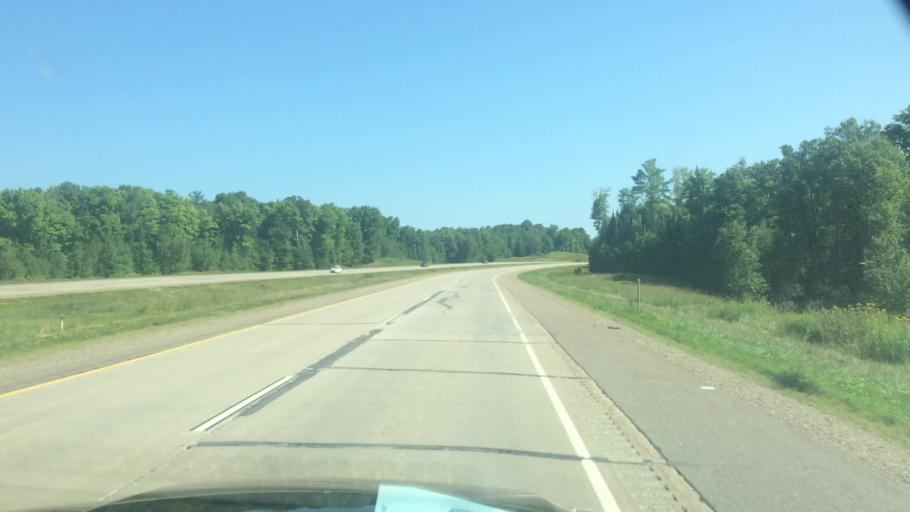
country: US
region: Wisconsin
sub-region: Lincoln County
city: Merrill
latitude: 45.3250
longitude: -89.6806
